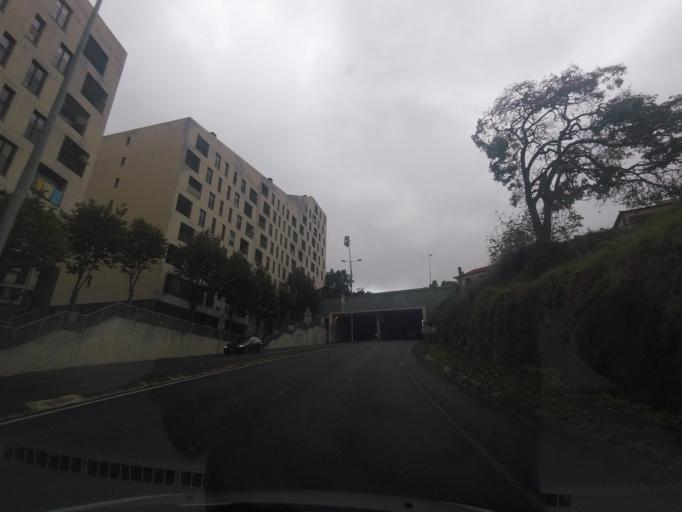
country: PT
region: Madeira
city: Camara de Lobos
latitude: 32.6493
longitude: -16.9403
